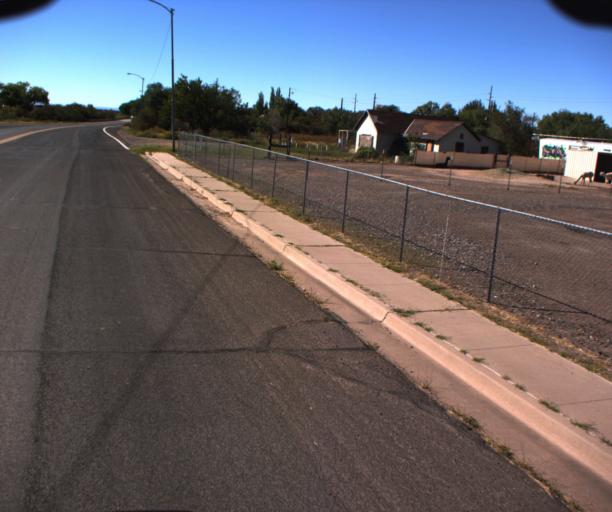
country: US
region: Arizona
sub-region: Navajo County
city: Joseph City
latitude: 34.9561
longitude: -110.3381
